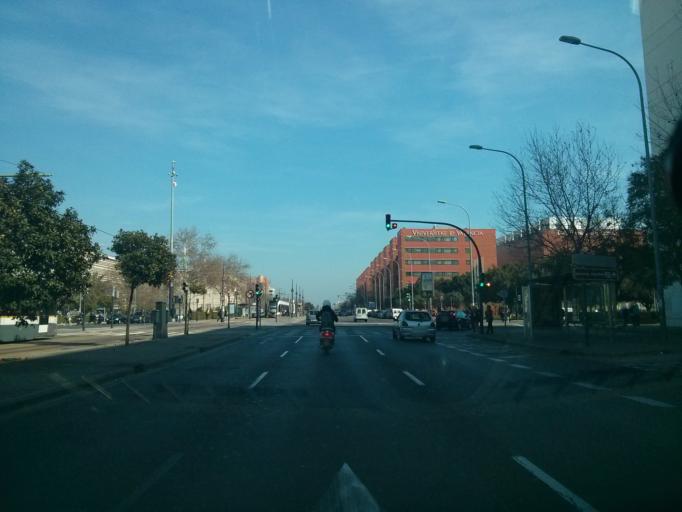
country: ES
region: Valencia
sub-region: Provincia de Valencia
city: Alboraya
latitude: 39.4800
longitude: -0.3461
